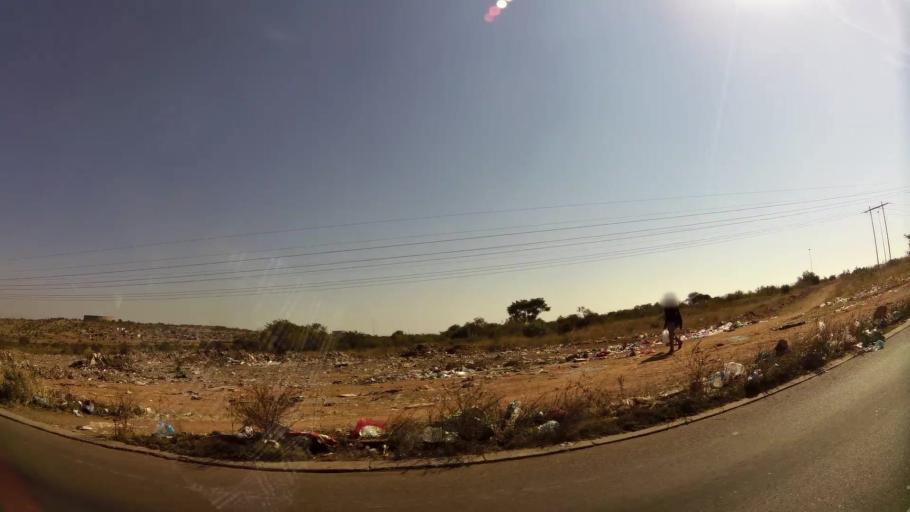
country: ZA
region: Gauteng
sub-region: City of Tshwane Metropolitan Municipality
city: Mabopane
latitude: -25.5256
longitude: 28.0866
